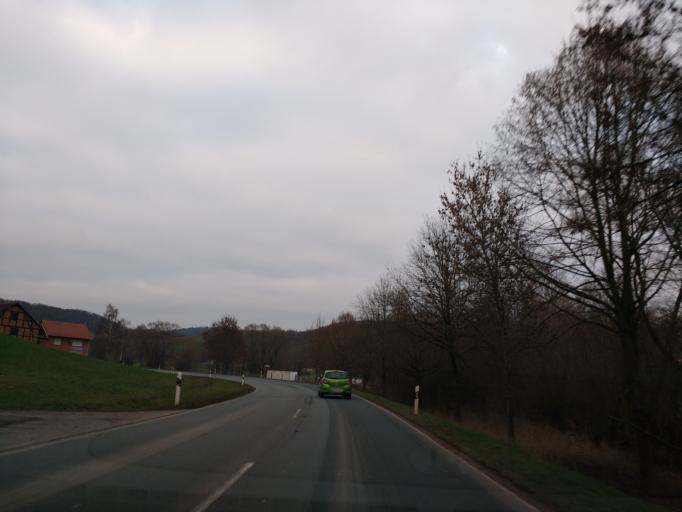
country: DE
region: Hesse
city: Bebra
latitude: 51.0146
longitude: 9.7750
